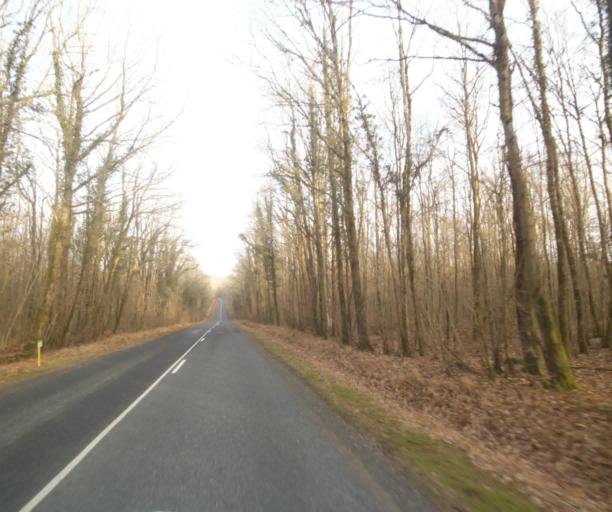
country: FR
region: Champagne-Ardenne
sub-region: Departement de la Haute-Marne
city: Bettancourt-la-Ferree
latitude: 48.6747
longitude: 4.9422
